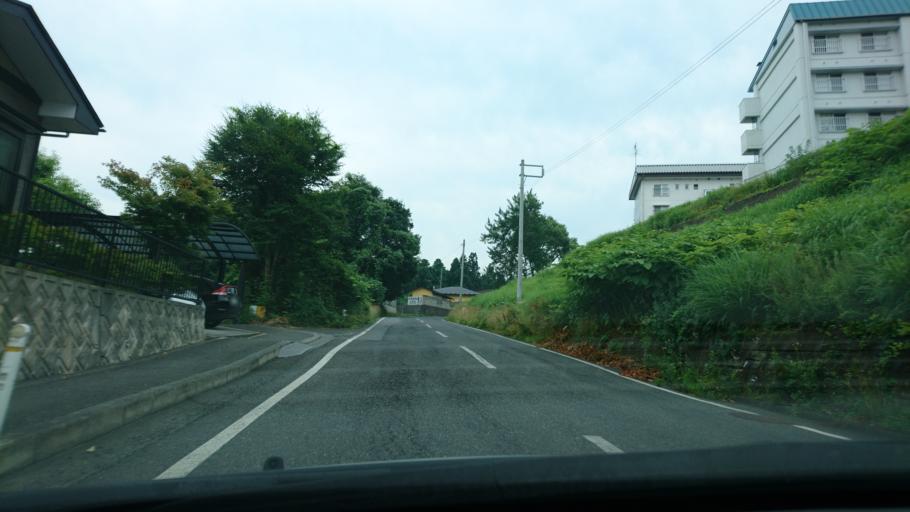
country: JP
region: Iwate
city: Ichinoseki
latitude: 38.9176
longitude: 141.1486
